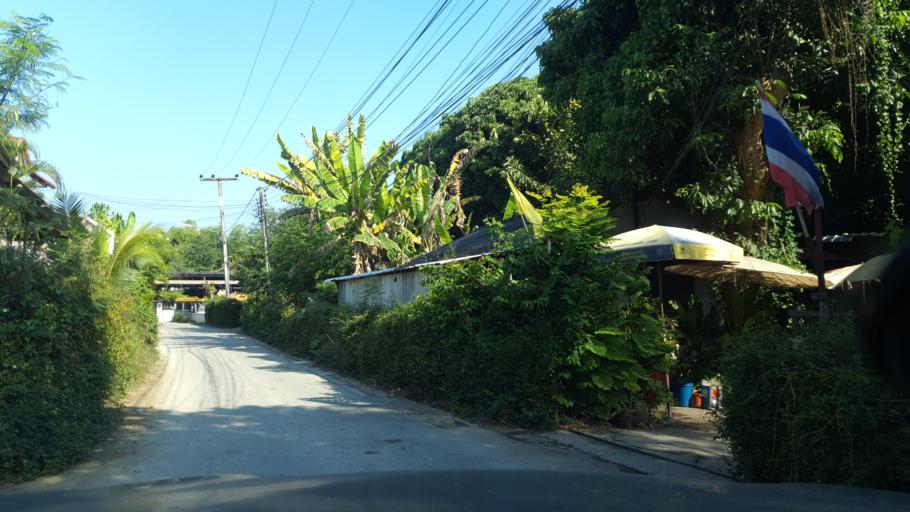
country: TH
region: Chiang Mai
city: Saraphi
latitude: 18.7170
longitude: 99.0724
